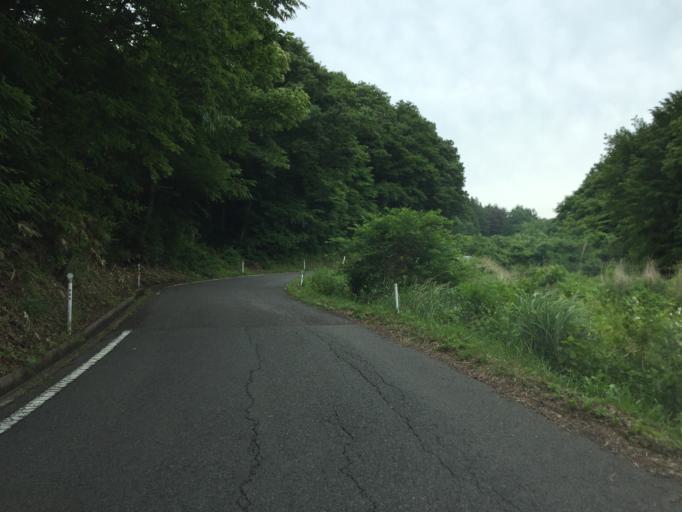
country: JP
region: Fukushima
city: Funehikimachi-funehiki
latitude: 37.4207
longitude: 140.7182
